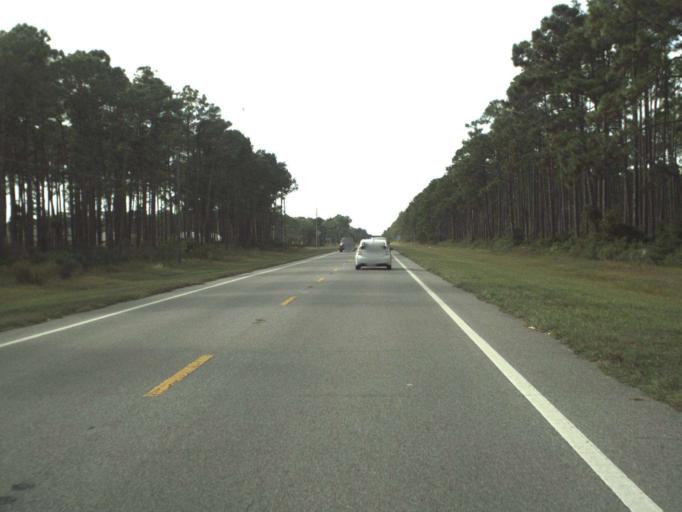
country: US
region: Florida
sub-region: Bay County
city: Tyndall Air Force Base
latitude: 30.0294
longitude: -85.5375
